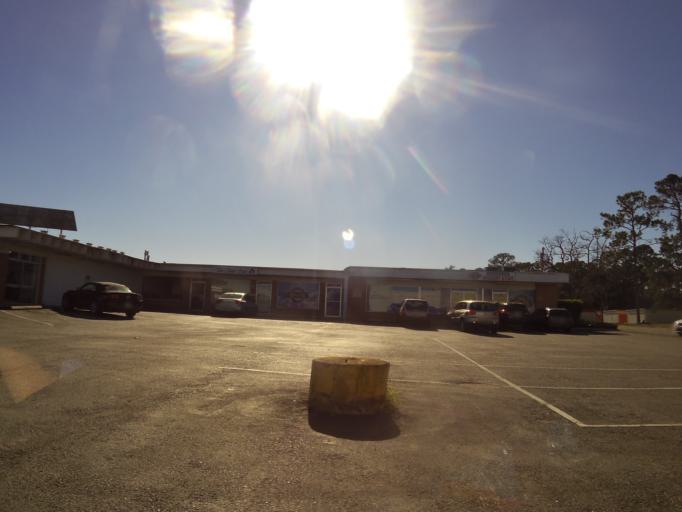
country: US
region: Florida
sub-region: Duval County
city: Jacksonville
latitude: 30.2753
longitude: -81.6066
